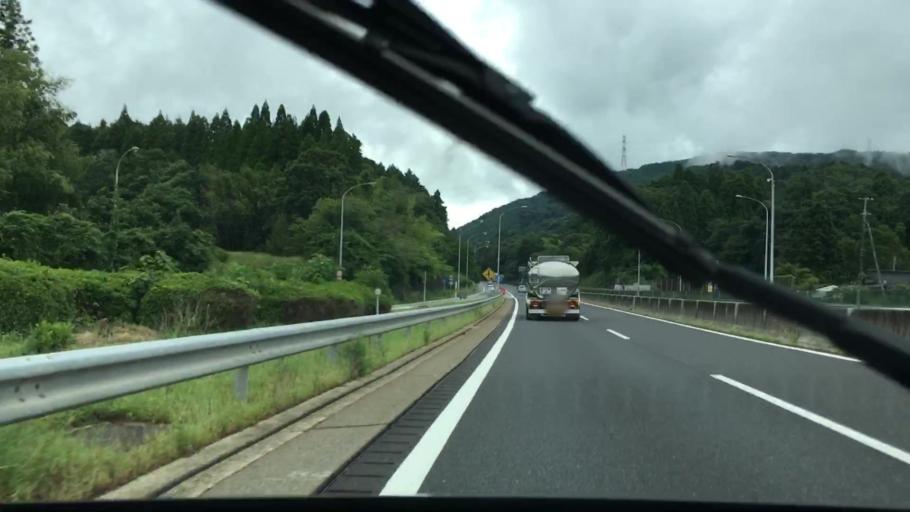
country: JP
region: Hyogo
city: Yamazakicho-nakabirose
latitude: 35.0317
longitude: 134.4856
